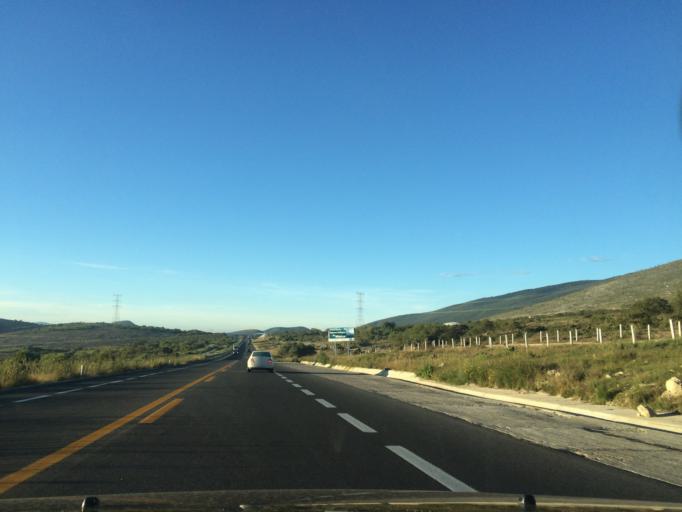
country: MX
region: Puebla
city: Morelos Canada
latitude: 18.7105
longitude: -97.4691
